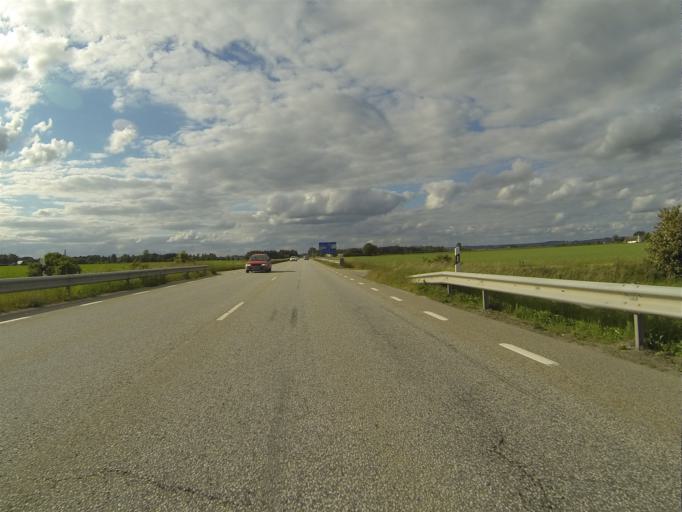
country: SE
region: Skane
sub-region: Staffanstorps Kommun
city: Staffanstorp
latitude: 55.6345
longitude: 13.2376
